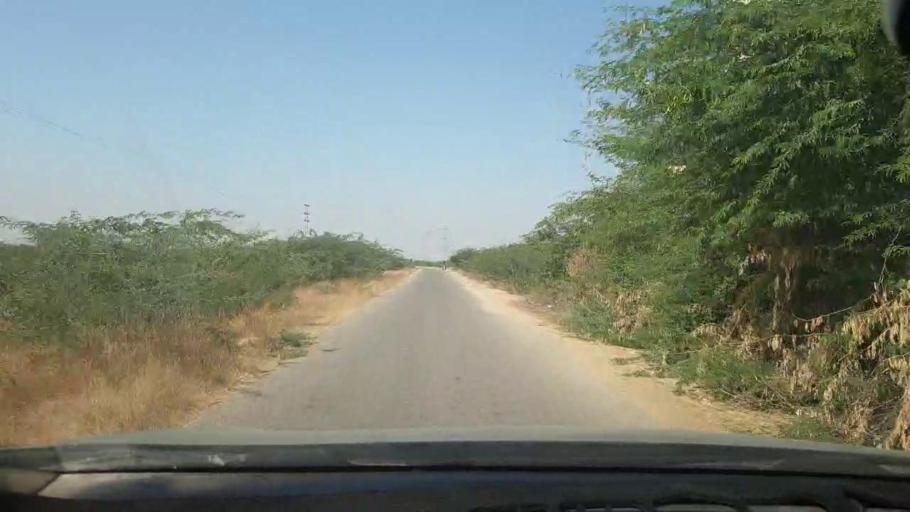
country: PK
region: Sindh
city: Malir Cantonment
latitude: 25.1621
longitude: 67.1544
